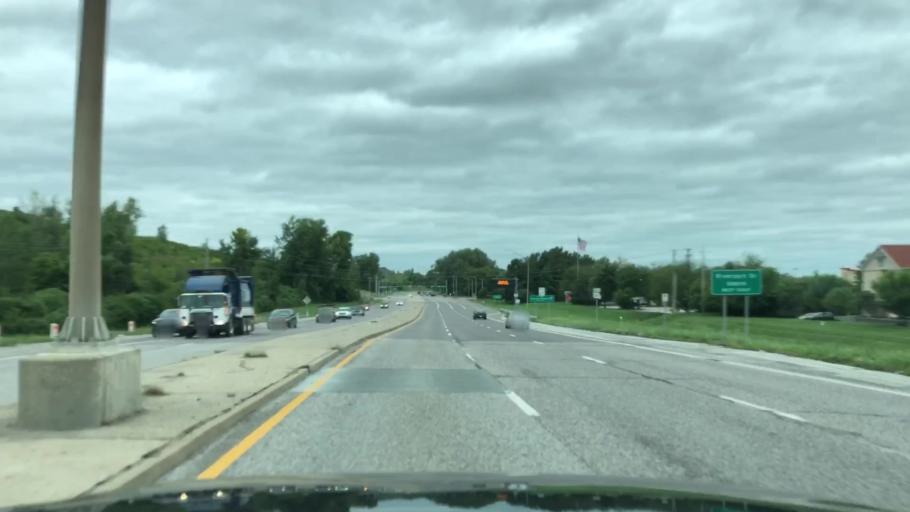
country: US
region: Missouri
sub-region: Saint Charles County
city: Saint Charles
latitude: 38.7522
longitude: -90.4608
